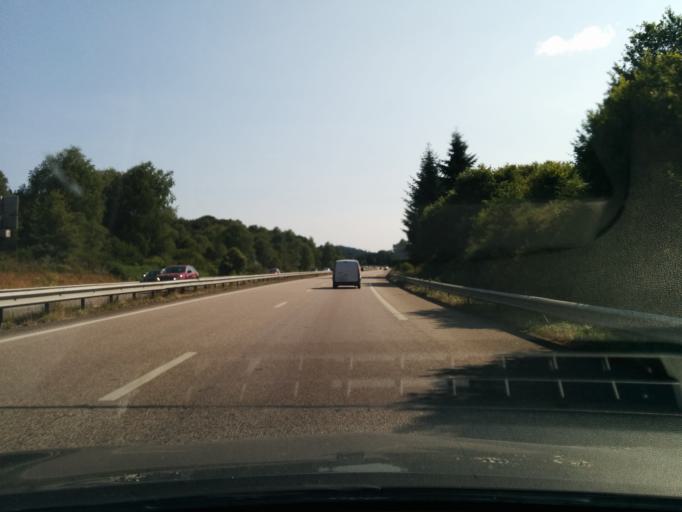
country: FR
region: Limousin
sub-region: Departement de la Haute-Vienne
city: Compreignac
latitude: 45.9783
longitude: 1.3251
